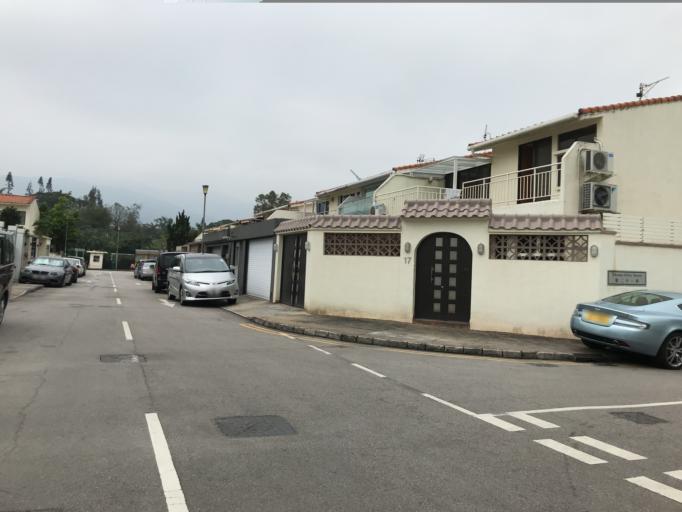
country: HK
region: Tai Po
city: Tai Po
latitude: 22.4653
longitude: 114.1533
